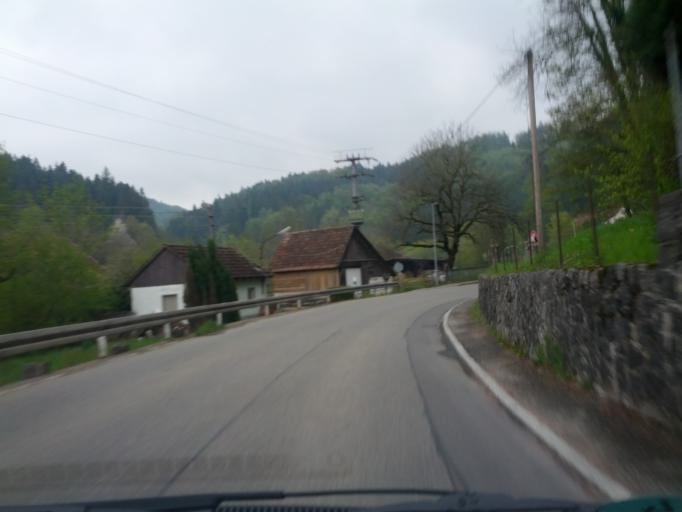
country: DE
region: Baden-Wuerttemberg
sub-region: Freiburg Region
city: Hausen
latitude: 47.6897
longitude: 7.7979
